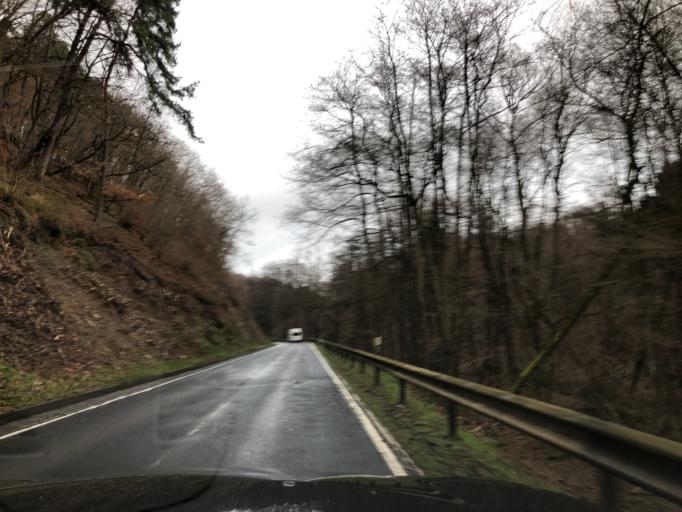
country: DE
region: Rheinland-Pfalz
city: Kasbach-Ohlenberg
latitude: 50.6124
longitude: 7.2821
